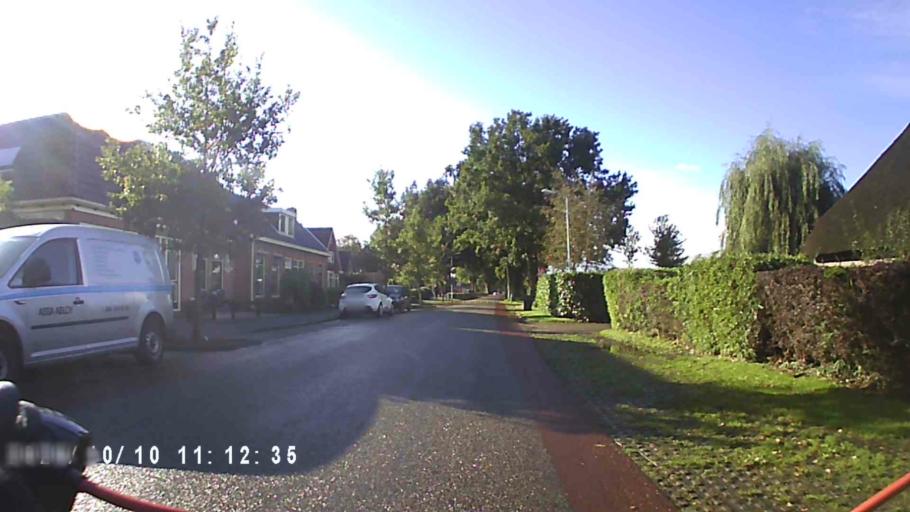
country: NL
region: Friesland
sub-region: Gemeente Smallingerland
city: Drachtstercompagnie
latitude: 53.1113
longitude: 6.2065
